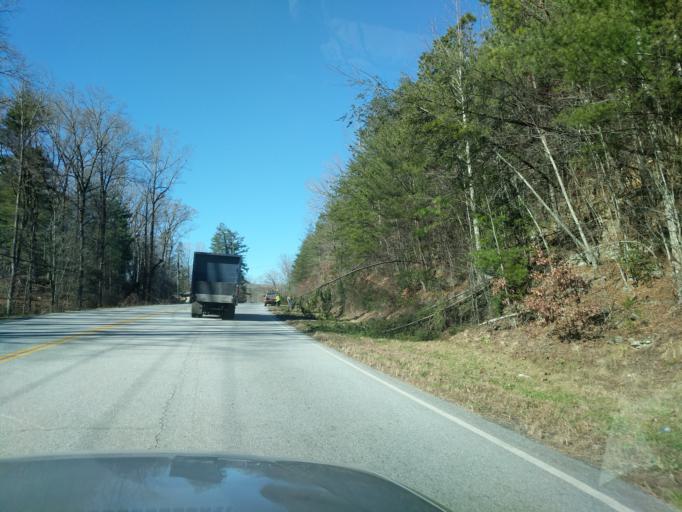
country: US
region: Georgia
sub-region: Rabun County
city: Clayton
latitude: 34.8605
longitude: -83.3874
